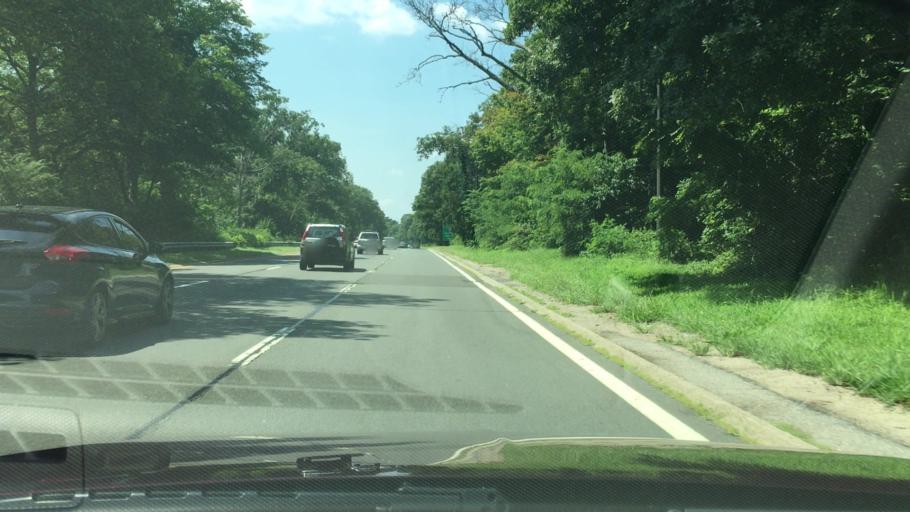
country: US
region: New York
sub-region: Suffolk County
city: Bay Wood
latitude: 40.7332
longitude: -73.3022
